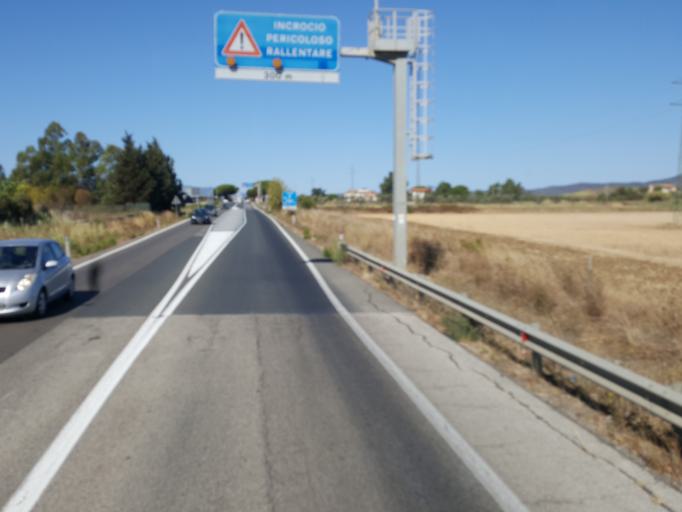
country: IT
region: Tuscany
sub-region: Provincia di Grosseto
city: Capalbio
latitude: 42.4150
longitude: 11.3777
